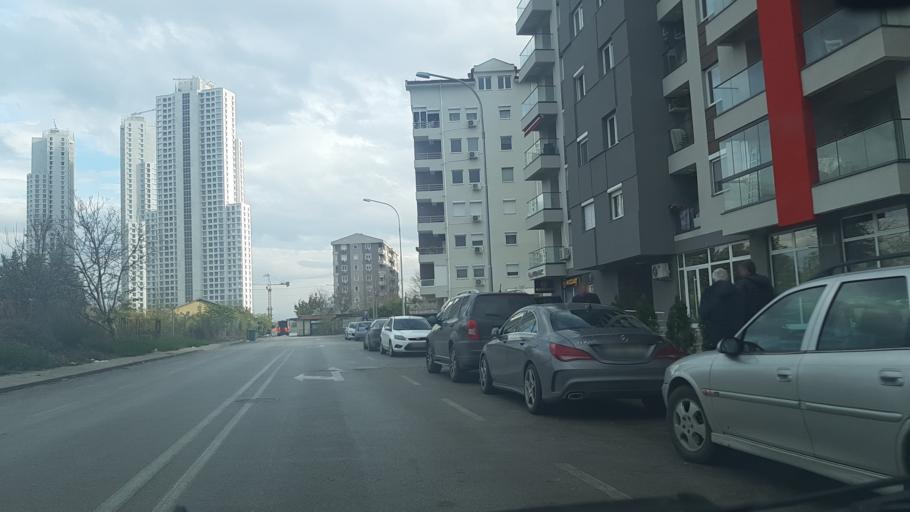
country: MK
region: Kisela Voda
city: Usje
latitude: 41.9807
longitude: 21.4600
